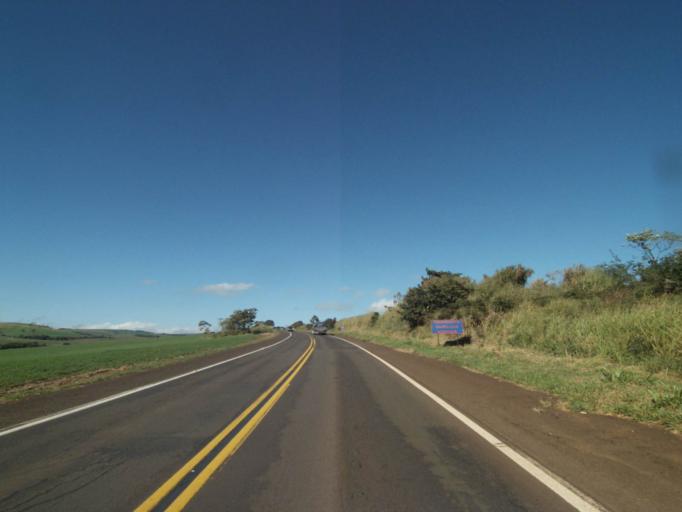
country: BR
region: Parana
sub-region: Faxinal
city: Faxinal
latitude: -23.8357
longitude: -51.1643
